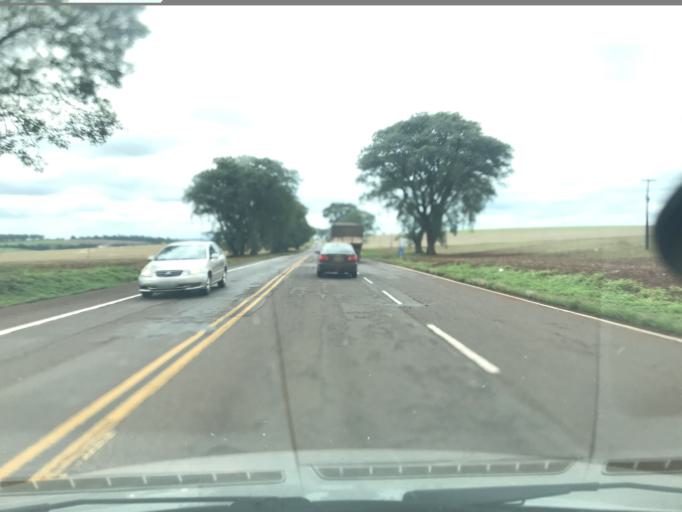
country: BR
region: Parana
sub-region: Terra Boa
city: Terra Boa
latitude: -23.6101
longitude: -52.4218
